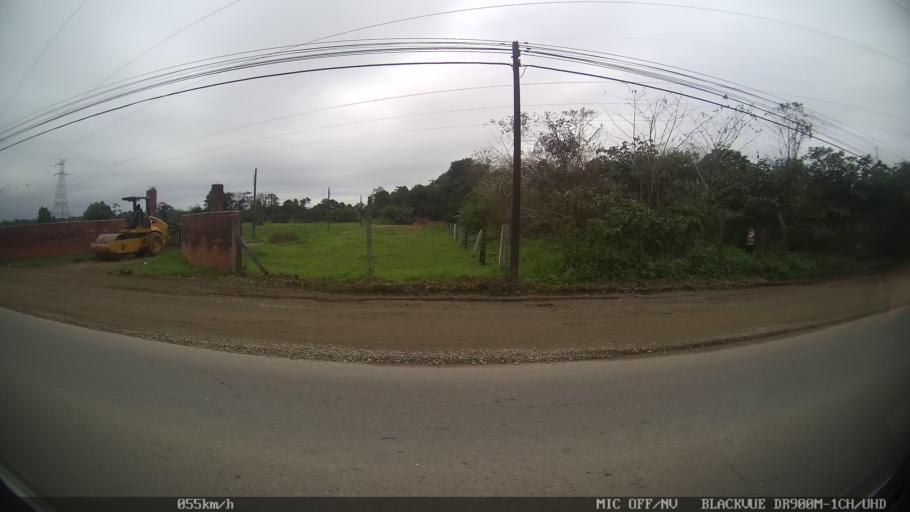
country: BR
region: Santa Catarina
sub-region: Joinville
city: Joinville
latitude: -26.2370
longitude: -48.8941
